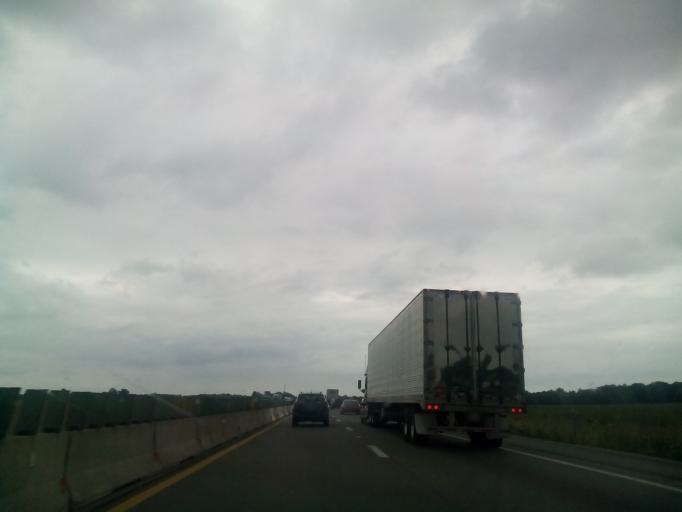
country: US
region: Ohio
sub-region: Huron County
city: Bellevue
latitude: 41.3514
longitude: -82.8549
